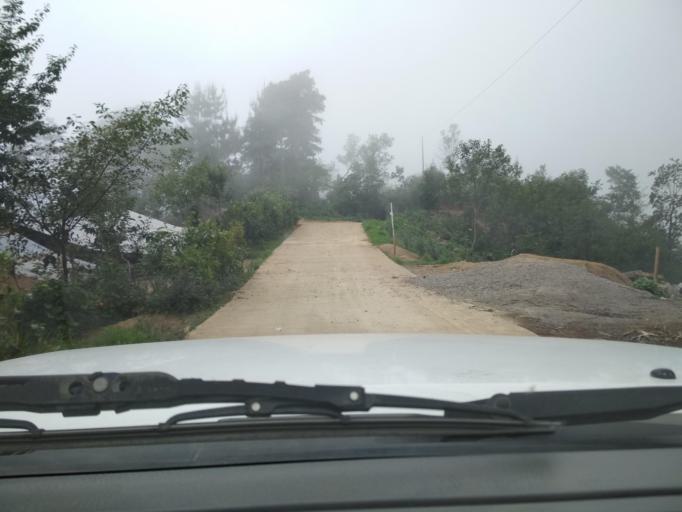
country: MX
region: Veracruz
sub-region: La Perla
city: Metlac Hernandez (Metlac Primero)
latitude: 18.9687
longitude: -97.1509
